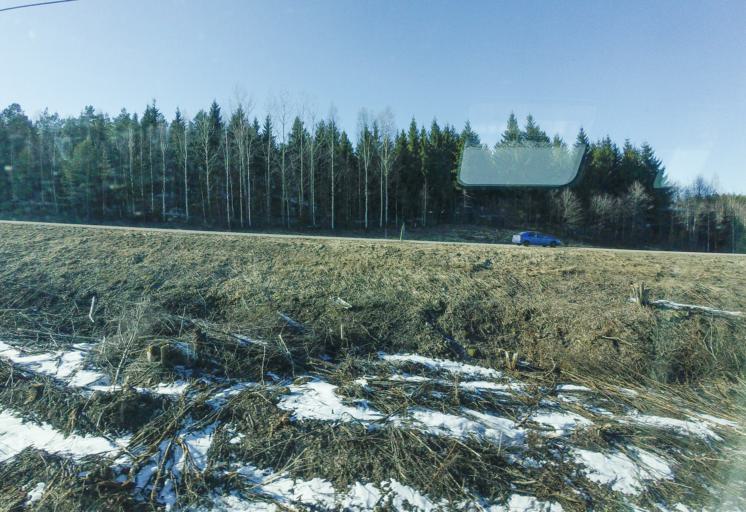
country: FI
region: South Karelia
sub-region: Imatra
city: Parikkala
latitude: 61.5062
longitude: 29.4982
